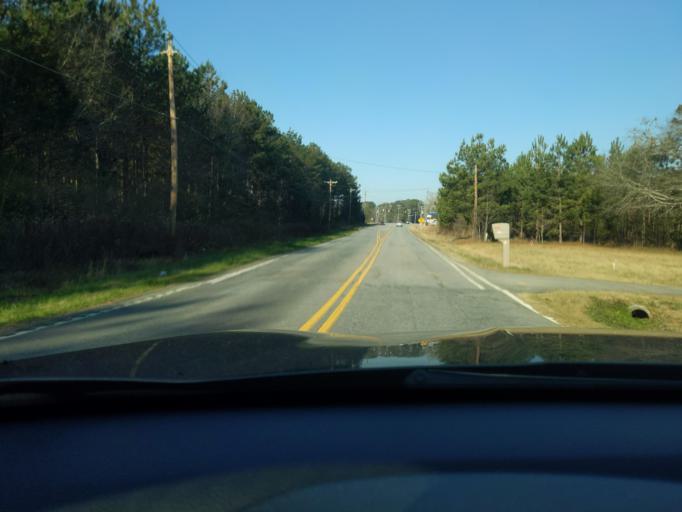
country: US
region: South Carolina
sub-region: Greenwood County
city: Greenwood
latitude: 34.1824
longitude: -82.1058
